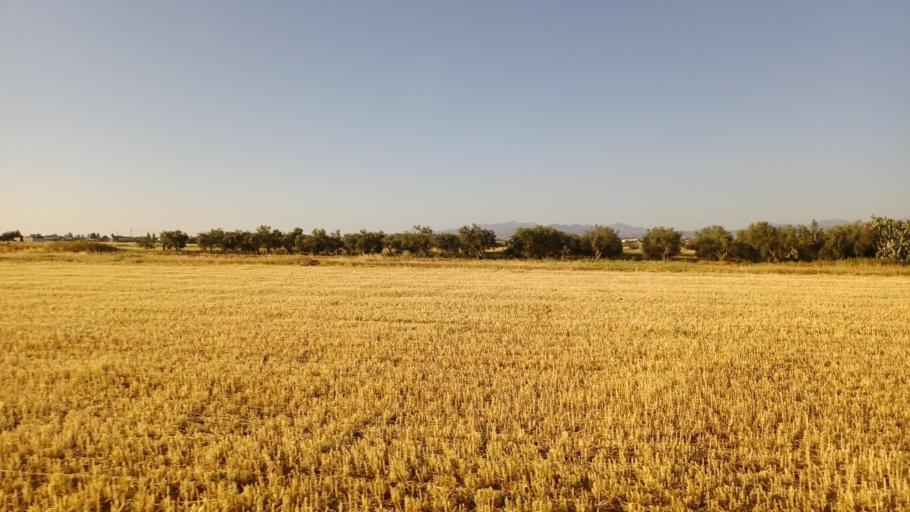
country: CY
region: Lefkosia
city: Kokkinotrimithia
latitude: 35.1420
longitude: 33.1898
